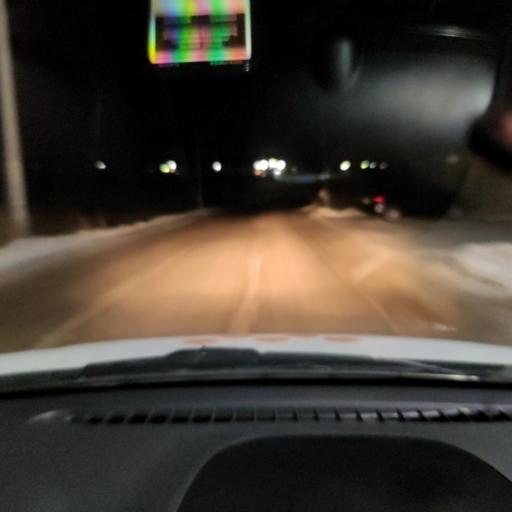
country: RU
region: Tatarstan
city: Vysokaya Gora
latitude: 55.8052
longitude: 49.3772
